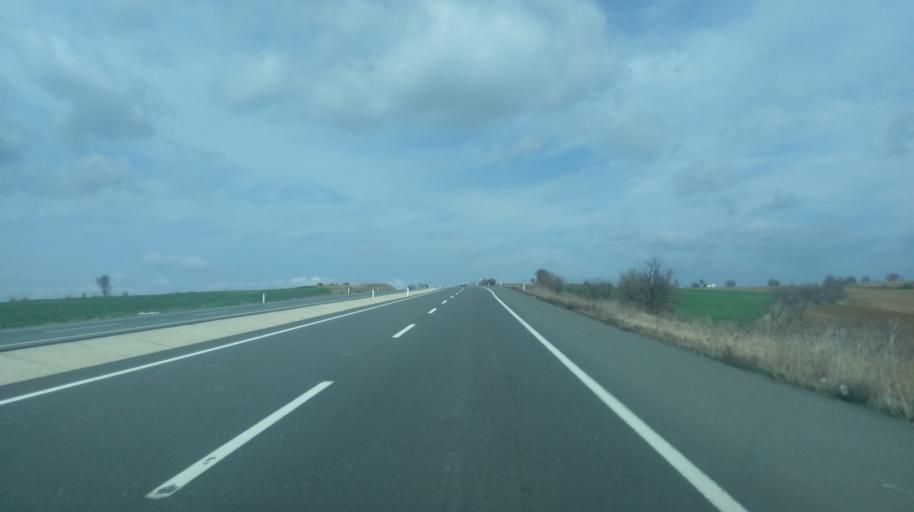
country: TR
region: Edirne
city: Hamidiye
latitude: 41.0570
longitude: 26.6399
